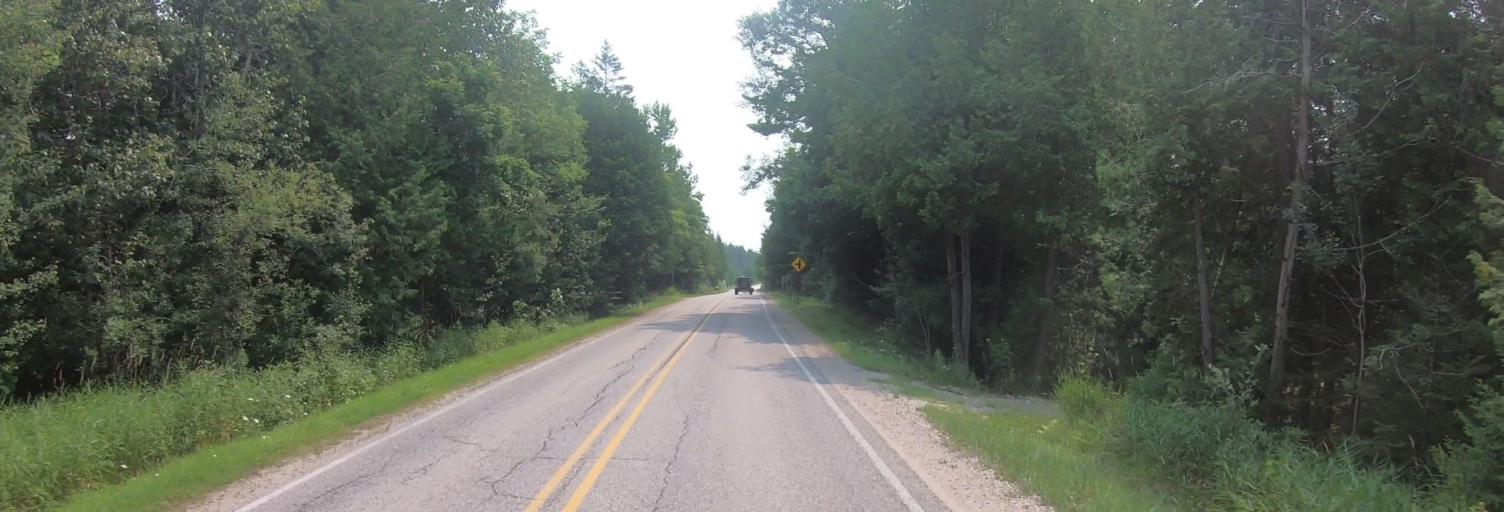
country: CA
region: Ontario
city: Thessalon
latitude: 45.9924
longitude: -83.7006
